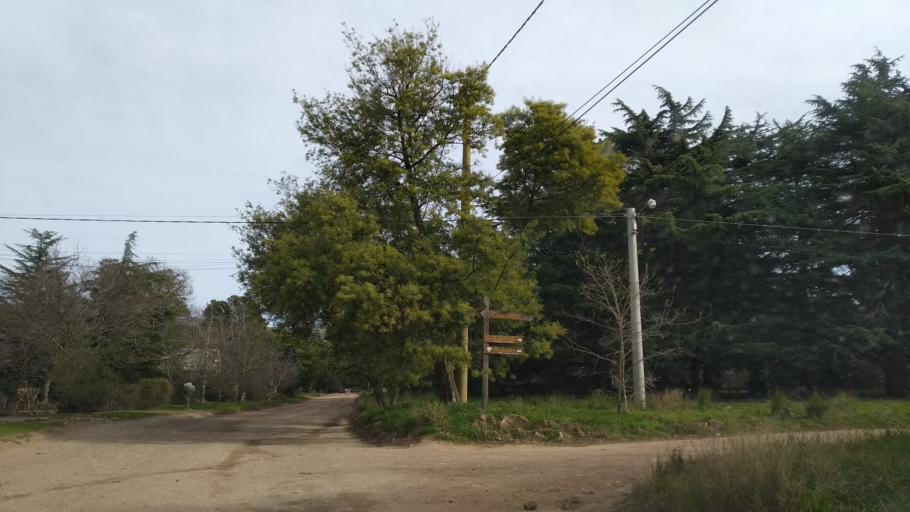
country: AR
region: Buenos Aires
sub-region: Partido de Tornquist
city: Tornquist
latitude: -38.0867
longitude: -61.9322
